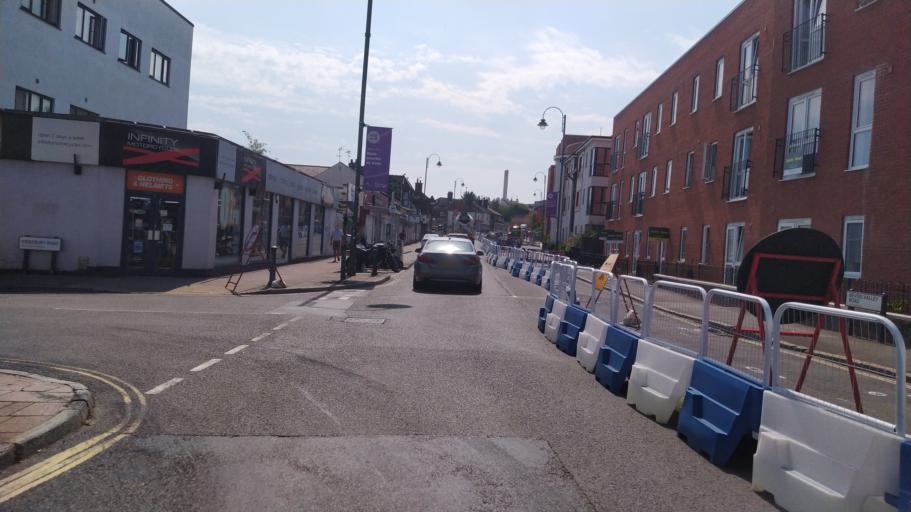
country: GB
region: England
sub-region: Southampton
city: Southampton
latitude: 50.9172
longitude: -1.3957
